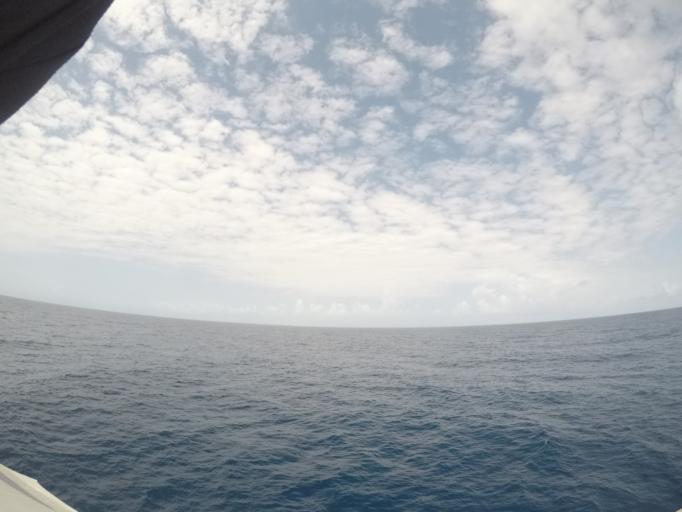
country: TZ
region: Zanzibar North
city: Nungwi
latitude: -5.5827
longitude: 39.3573
